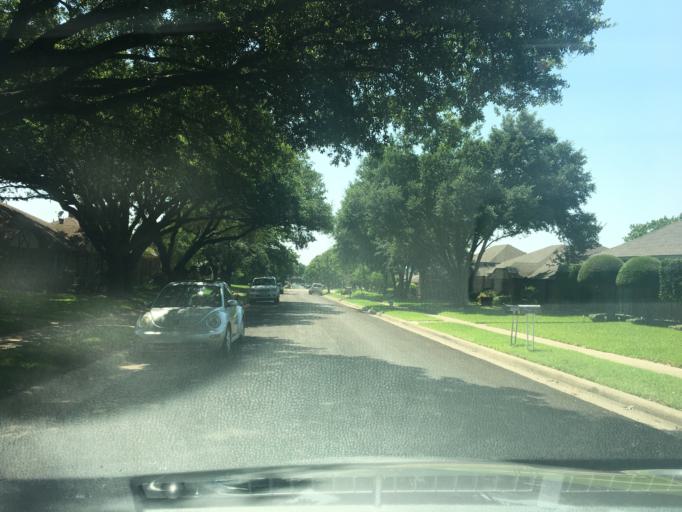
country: US
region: Texas
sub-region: Dallas County
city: Richardson
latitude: 32.9258
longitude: -96.7075
